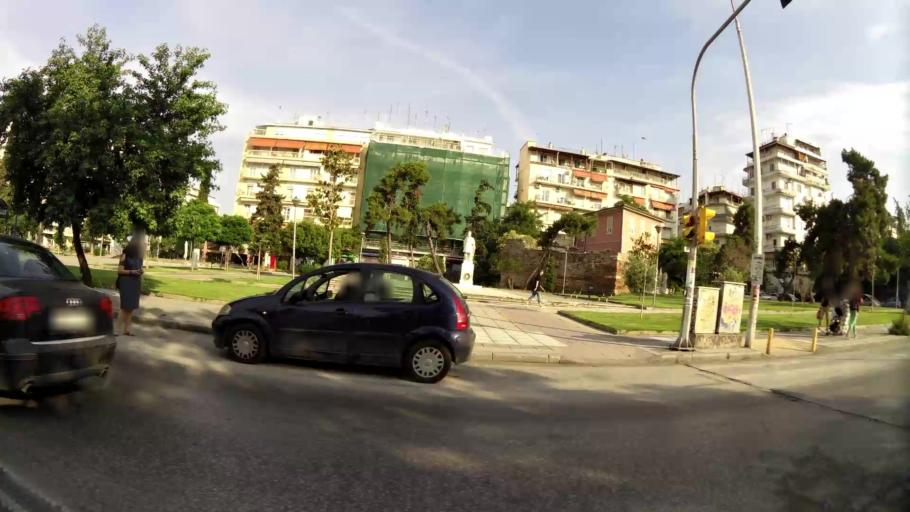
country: GR
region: Central Macedonia
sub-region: Nomos Thessalonikis
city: Agios Pavlos
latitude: 40.6326
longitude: 22.9547
